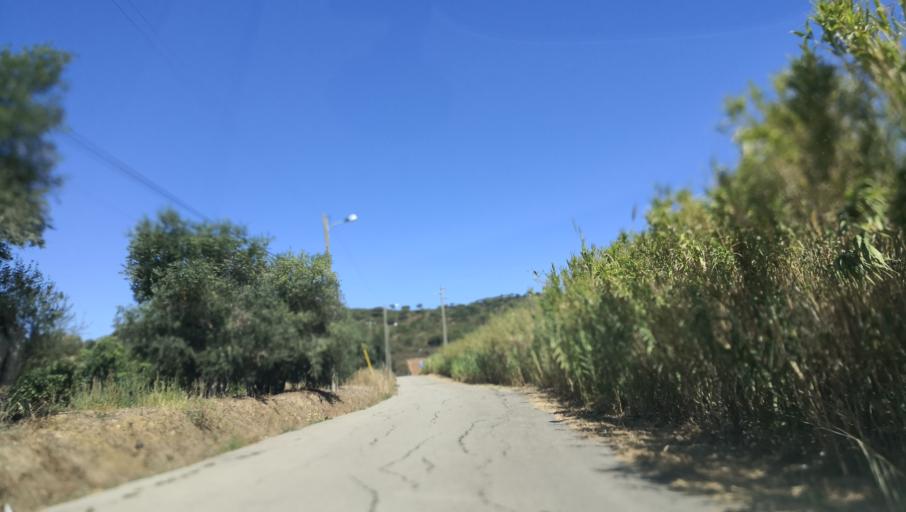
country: PT
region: Setubal
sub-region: Setubal
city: Setubal
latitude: 38.5347
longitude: -8.9141
